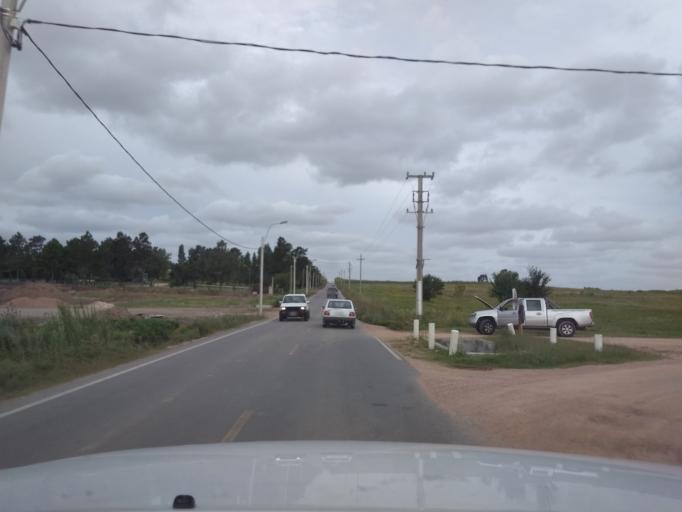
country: UY
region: Canelones
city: Colonia Nicolich
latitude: -34.7840
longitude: -56.0140
